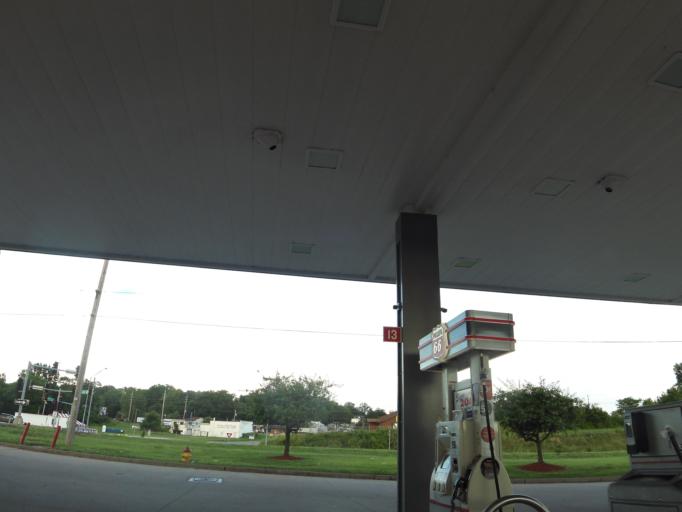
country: US
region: Missouri
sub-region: Jefferson County
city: Cedar Hill
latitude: 38.3549
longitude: -90.6496
